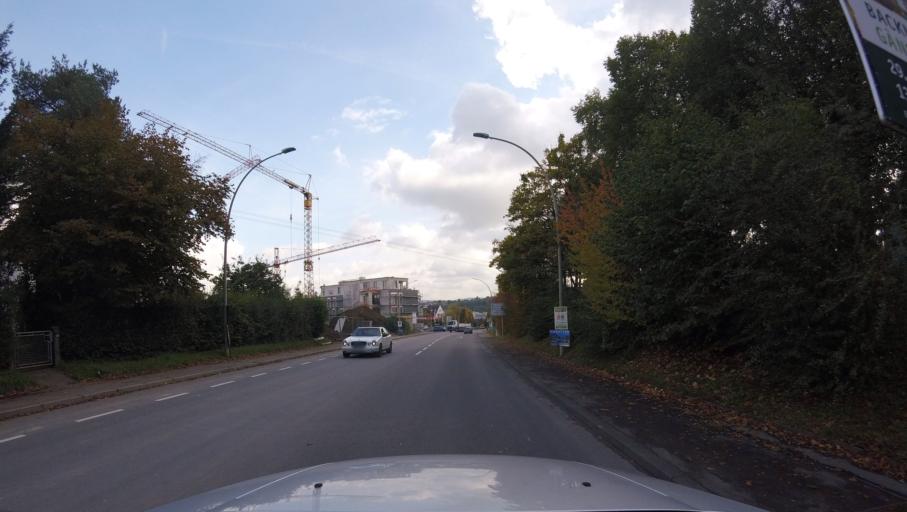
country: DE
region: Baden-Wuerttemberg
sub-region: Regierungsbezirk Stuttgart
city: Backnang
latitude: 48.9509
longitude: 9.4195
